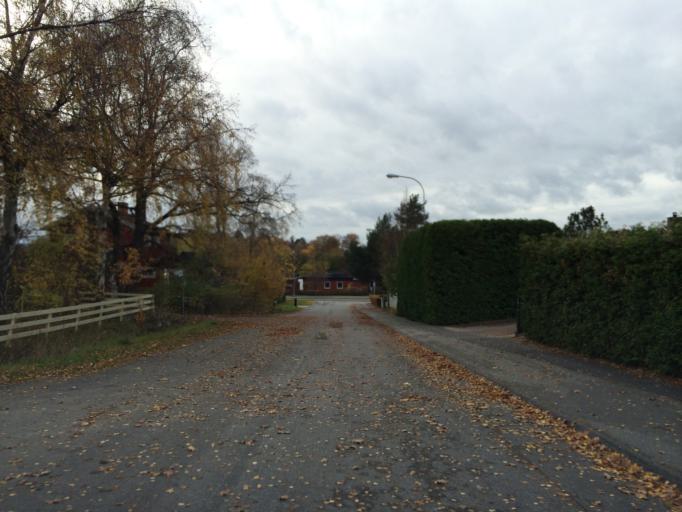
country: SE
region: Stockholm
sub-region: Sollentuna Kommun
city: Sollentuna
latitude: 59.4620
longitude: 17.9153
